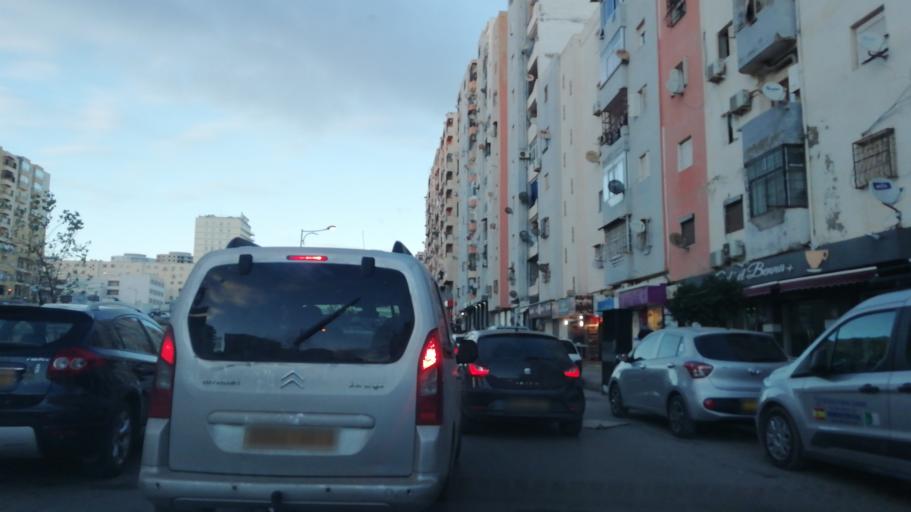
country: DZ
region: Oran
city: Bir el Djir
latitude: 35.7033
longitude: -0.5606
